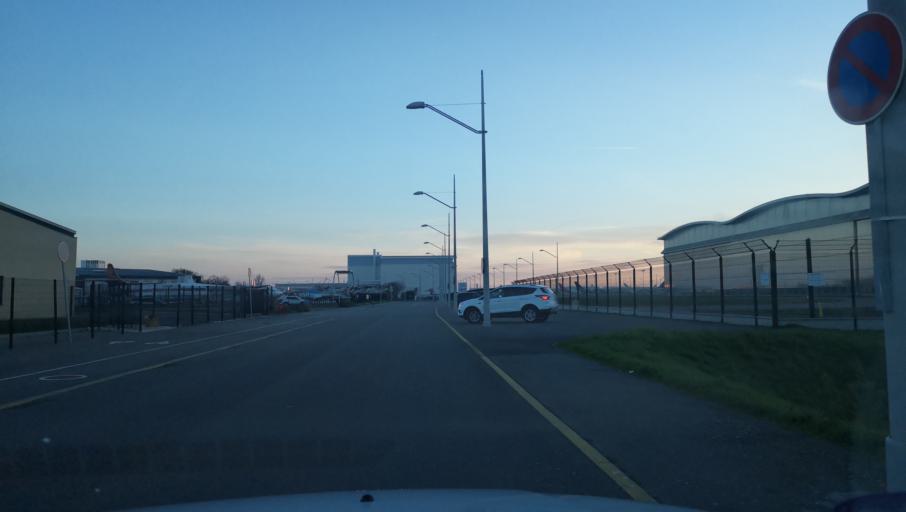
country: FR
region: Midi-Pyrenees
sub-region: Departement de la Haute-Garonne
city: Beauzelle
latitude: 43.6589
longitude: 1.3584
